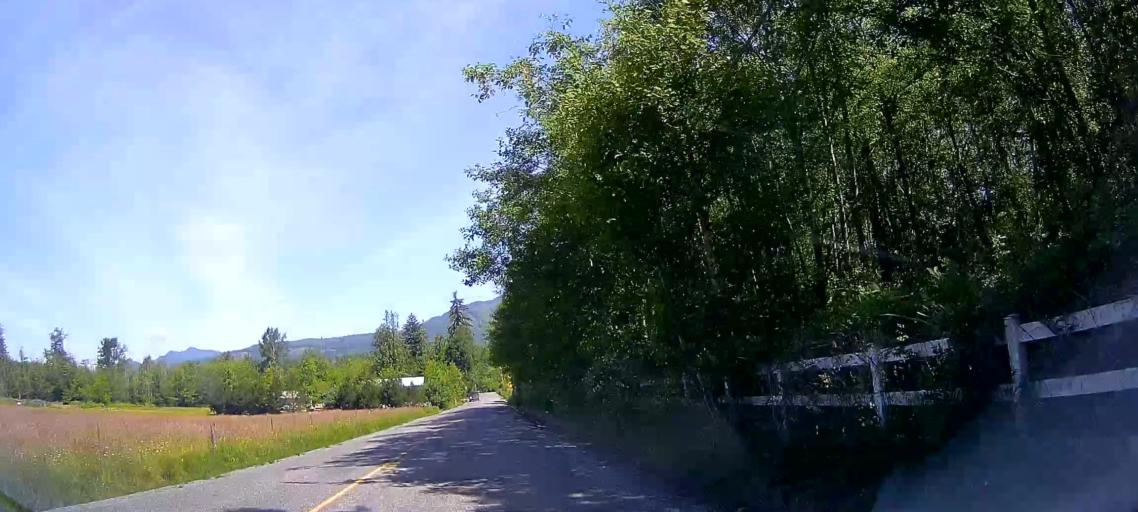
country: US
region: Washington
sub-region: Skagit County
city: Sedro-Woolley
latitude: 48.5558
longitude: -122.2684
